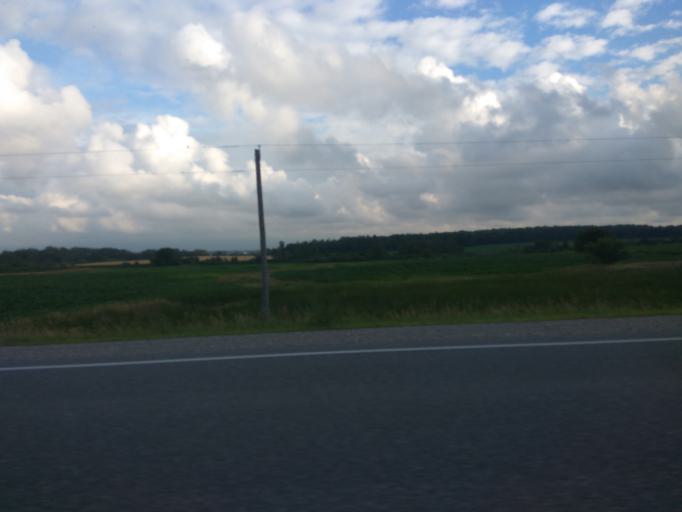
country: CA
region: Ontario
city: Stratford
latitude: 43.3692
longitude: -80.7959
